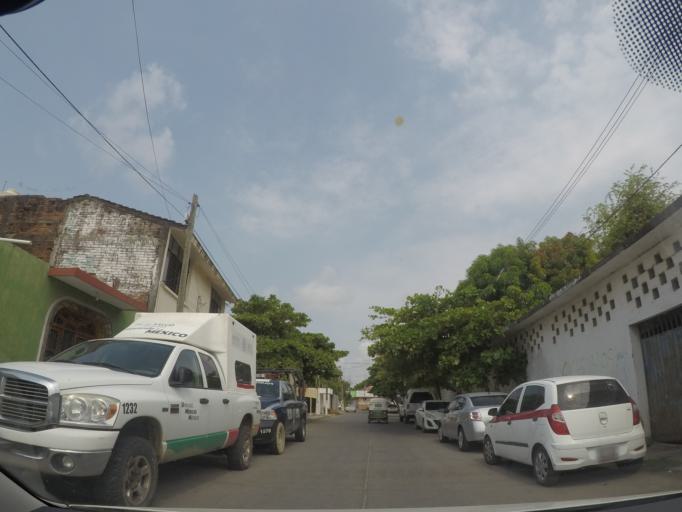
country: MX
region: Oaxaca
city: Juchitan de Zaragoza
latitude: 16.4436
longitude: -95.0235
